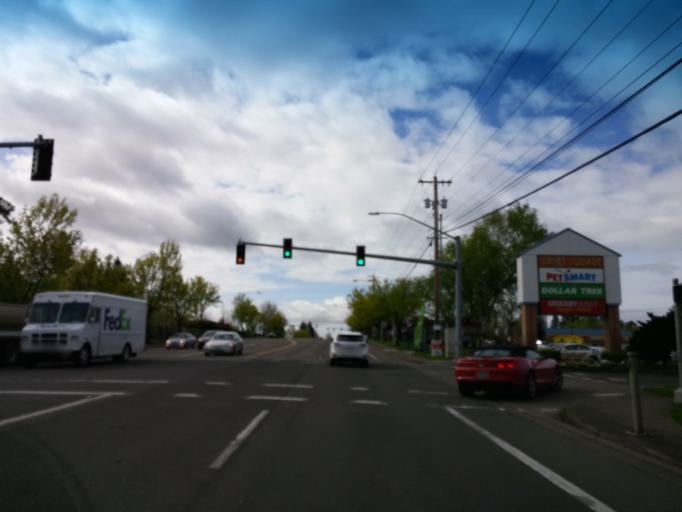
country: US
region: Oregon
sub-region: Washington County
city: Rockcreek
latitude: 45.5300
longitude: -122.8676
